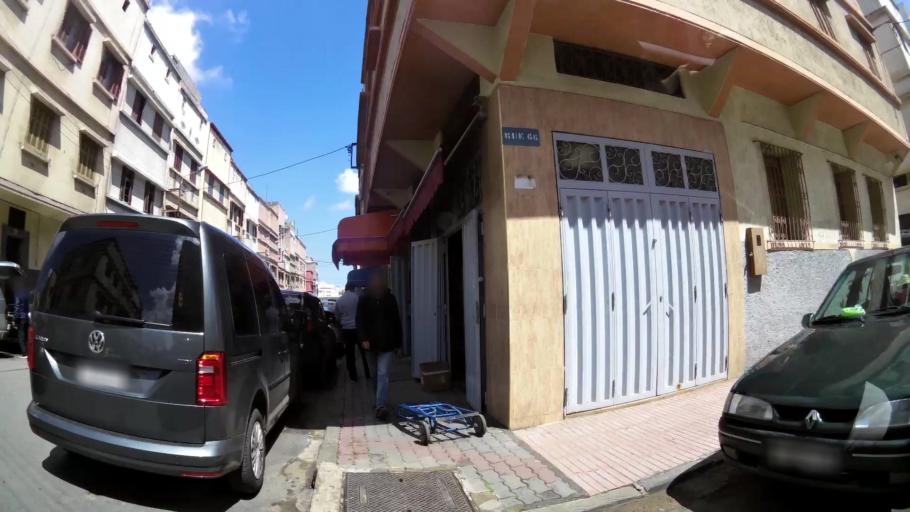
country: MA
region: Grand Casablanca
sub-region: Casablanca
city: Casablanca
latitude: 33.5604
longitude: -7.5998
